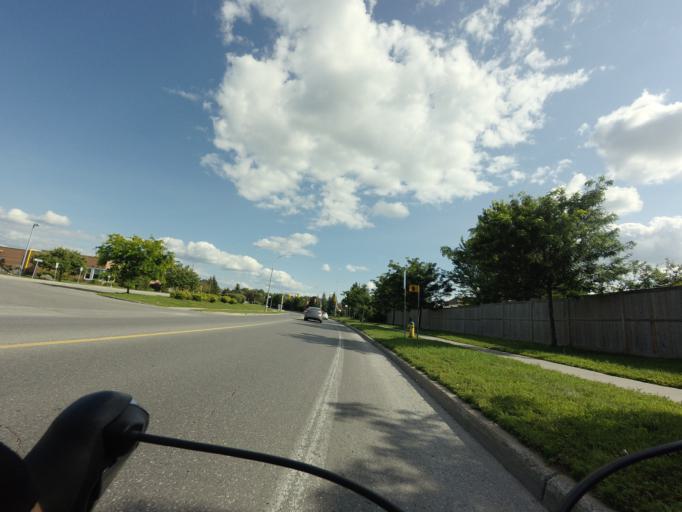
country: CA
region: Ontario
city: Bells Corners
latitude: 45.2824
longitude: -75.8454
